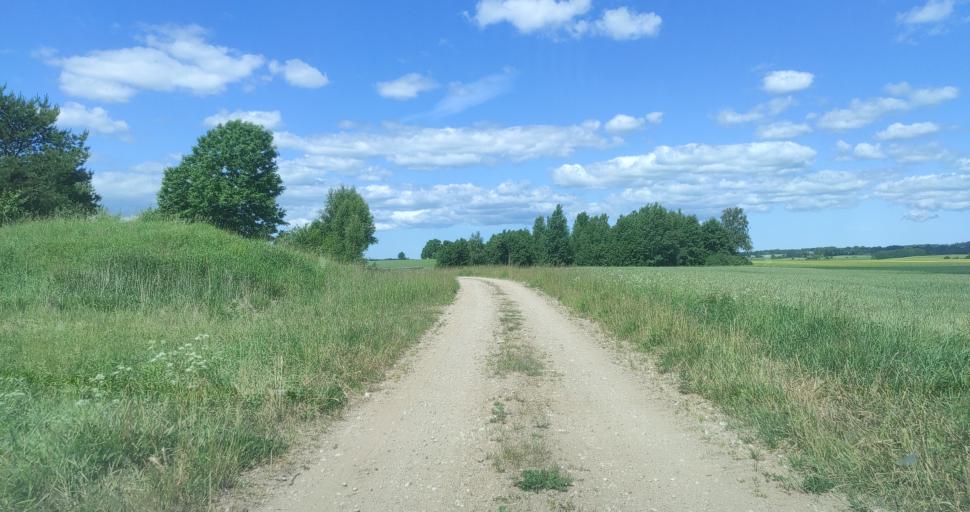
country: LV
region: Aizpute
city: Aizpute
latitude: 56.8557
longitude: 21.7164
